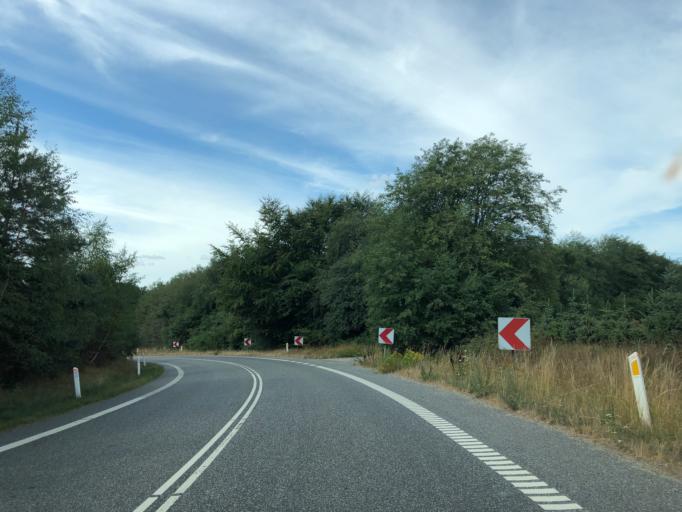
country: DK
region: Central Jutland
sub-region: Silkeborg Kommune
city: Silkeborg
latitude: 56.1421
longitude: 9.4233
